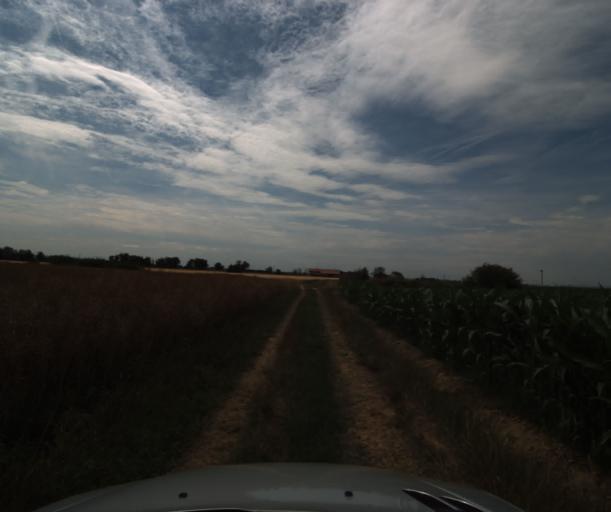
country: FR
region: Midi-Pyrenees
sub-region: Departement de la Haute-Garonne
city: Lacasse
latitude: 43.4154
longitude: 1.2625
